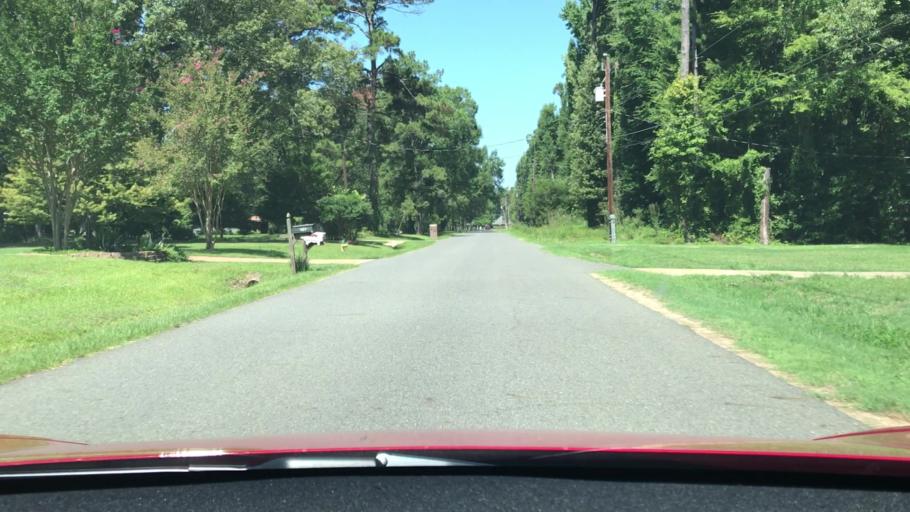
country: US
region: Louisiana
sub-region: De Soto Parish
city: Stonewall
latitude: 32.3448
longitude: -93.7098
